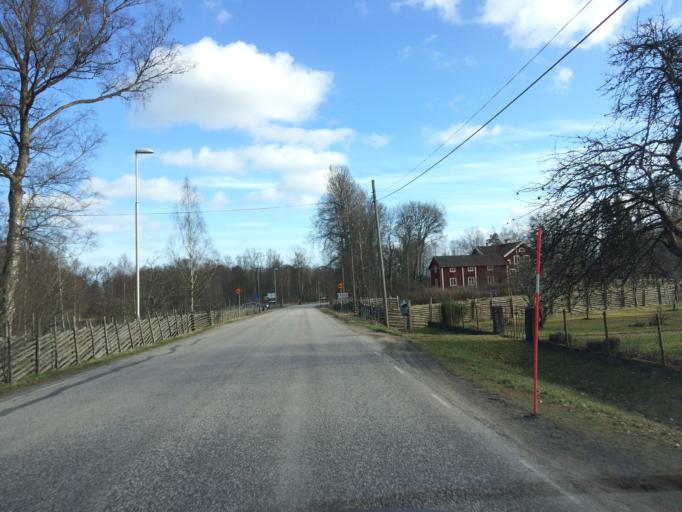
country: SE
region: Kronoberg
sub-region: Almhults Kommun
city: AElmhult
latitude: 56.5671
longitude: 14.1249
